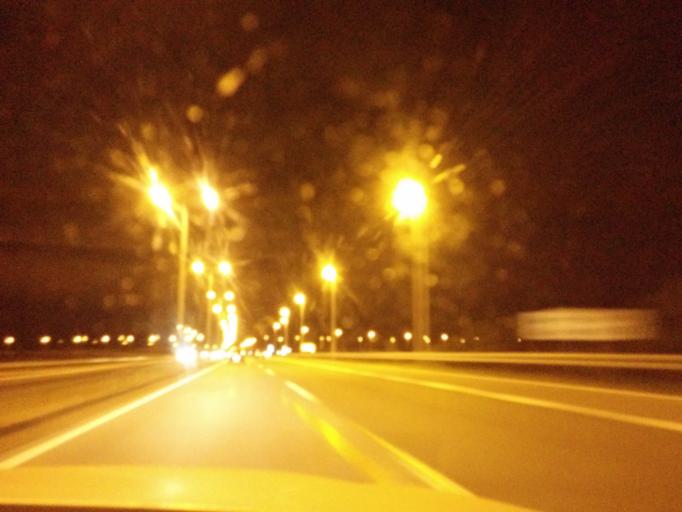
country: RS
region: Autonomna Pokrajina Vojvodina
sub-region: Sremski Okrug
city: Pecinci
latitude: 44.9215
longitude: 19.9575
